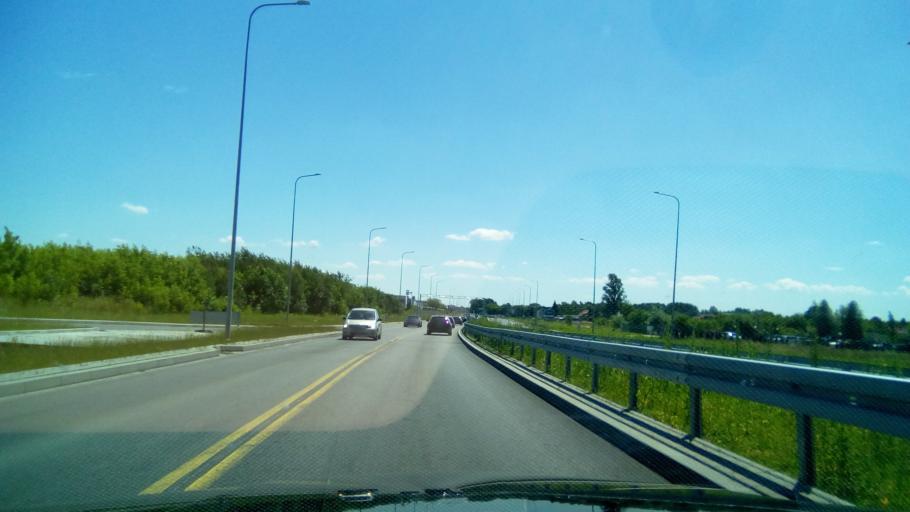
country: PL
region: Masovian Voivodeship
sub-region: Radom
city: Radom
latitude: 51.4184
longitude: 21.1918
